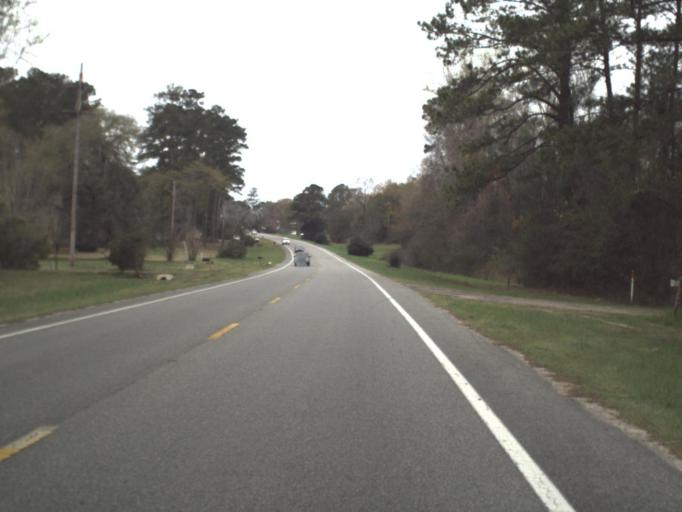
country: US
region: Florida
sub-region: Jefferson County
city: Monticello
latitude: 30.5445
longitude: -83.8467
